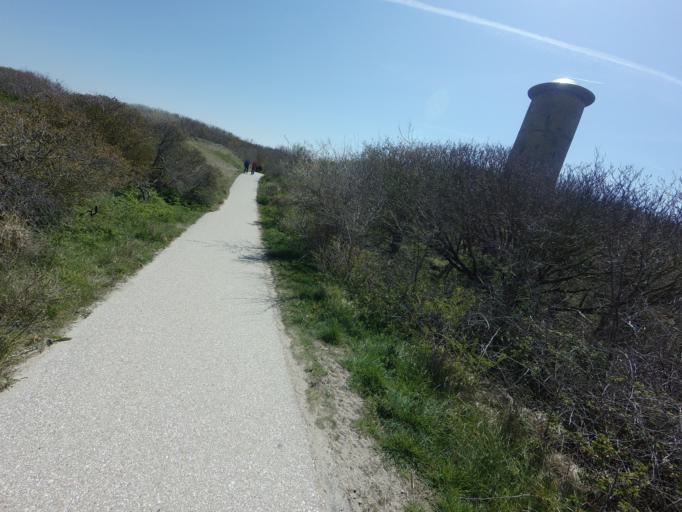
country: NL
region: Zeeland
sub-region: Gemeente Middelburg
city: Middelburg
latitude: 51.5674
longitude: 3.5014
